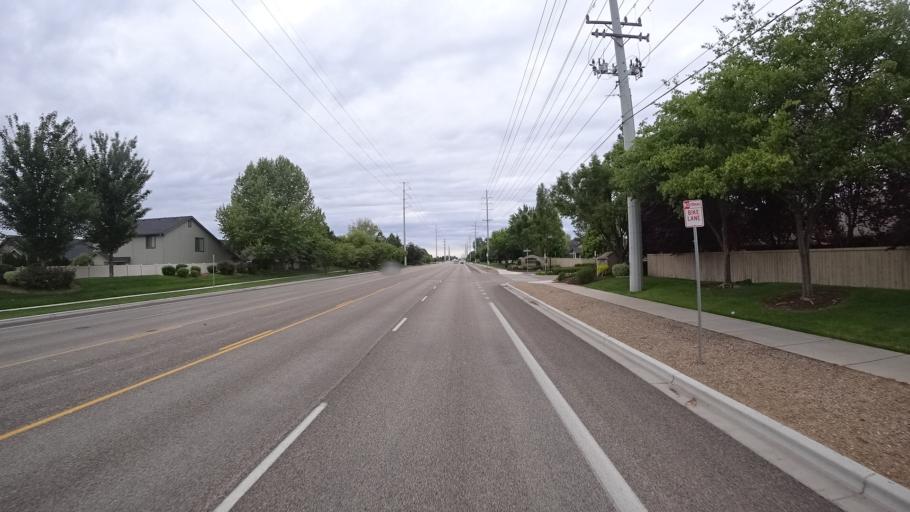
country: US
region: Idaho
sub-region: Ada County
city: Meridian
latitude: 43.6484
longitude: -116.3653
